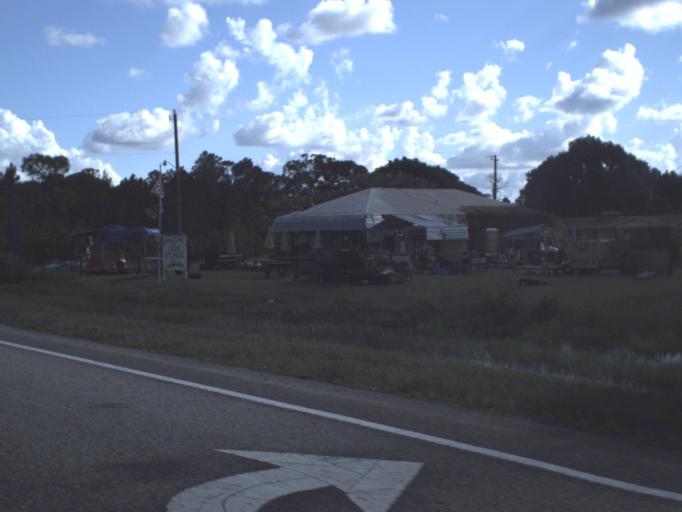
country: US
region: Florida
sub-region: Charlotte County
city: Charlotte Park
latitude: 26.8471
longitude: -81.9809
